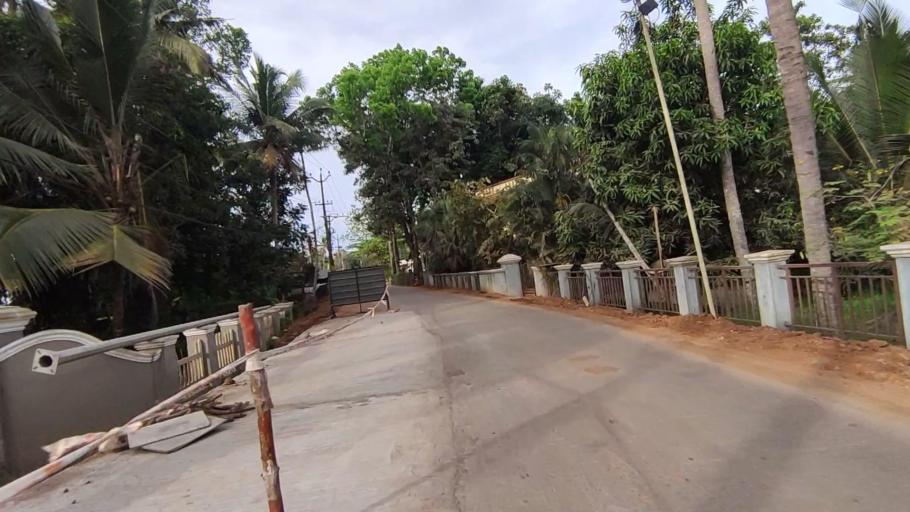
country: IN
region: Kerala
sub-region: Kottayam
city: Kottayam
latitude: 9.6085
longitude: 76.4907
